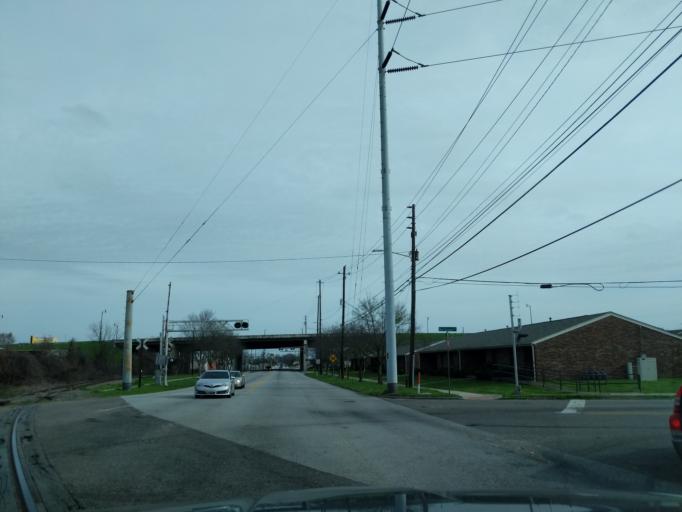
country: US
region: Georgia
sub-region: Richmond County
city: Augusta
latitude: 33.4615
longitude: -81.9680
